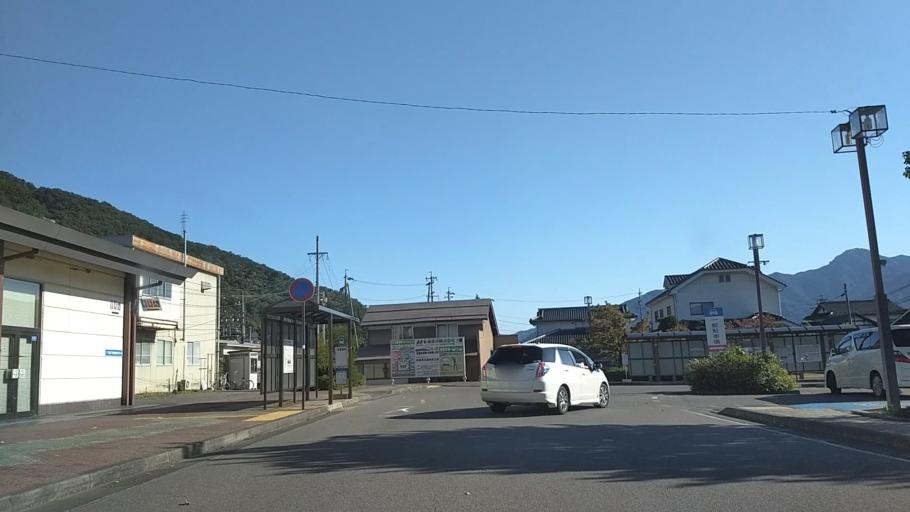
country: JP
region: Nagano
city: Nagano-shi
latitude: 36.5320
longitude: 138.1279
